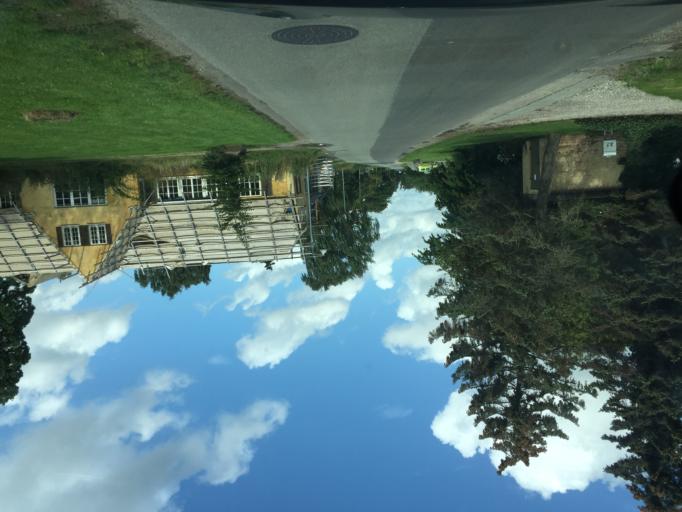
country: DK
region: South Denmark
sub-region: Odense Kommune
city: Stige
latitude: 55.4426
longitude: 10.3910
